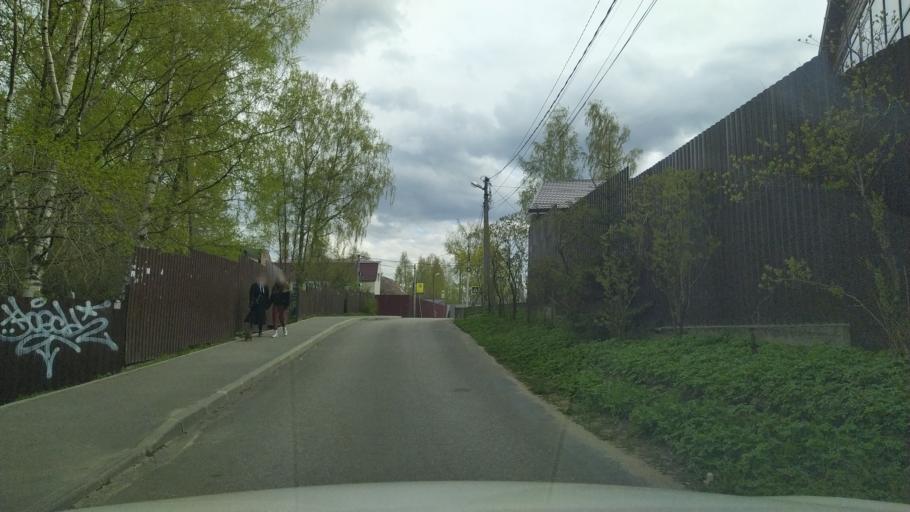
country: RU
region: Leningrad
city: Murino
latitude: 60.0458
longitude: 30.4418
